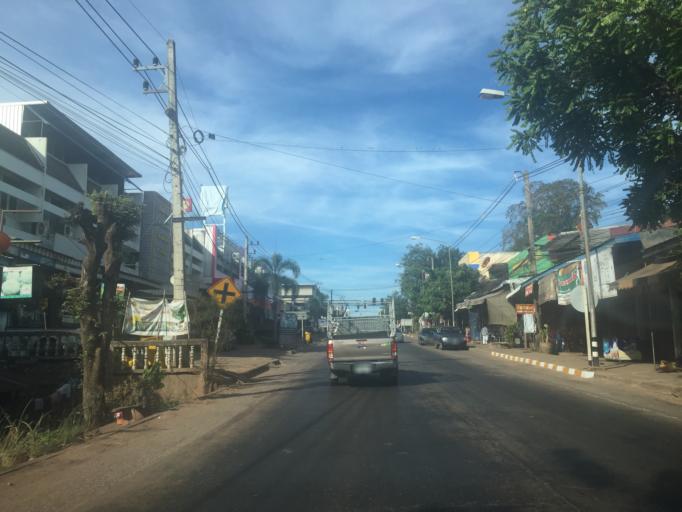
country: TH
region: Changwat Udon Thani
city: Kumphawapi
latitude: 17.1108
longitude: 103.0191
